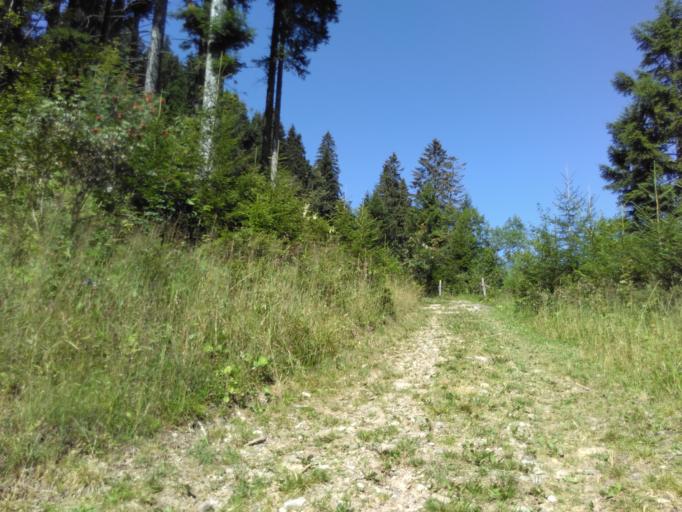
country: CH
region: Lucerne
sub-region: Lucerne-Land District
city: Vitznau
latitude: 47.0449
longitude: 8.4823
